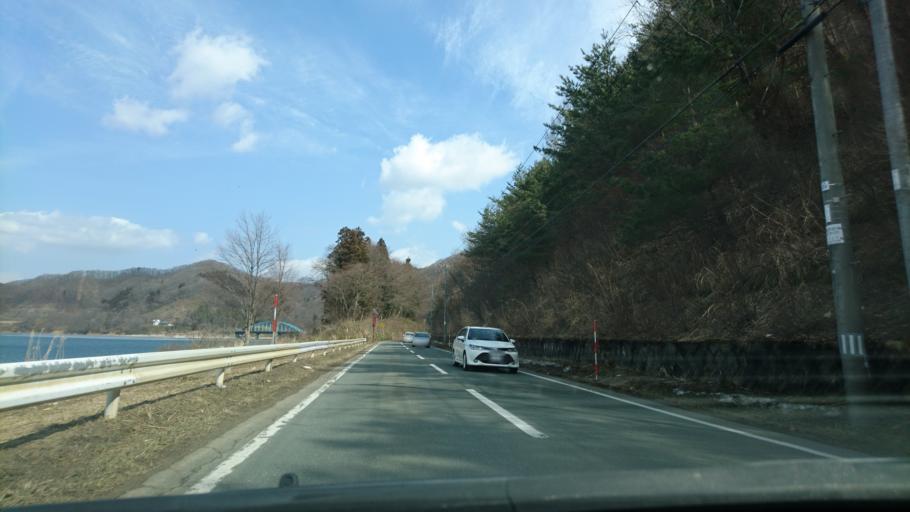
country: JP
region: Iwate
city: Shizukuishi
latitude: 39.6824
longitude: 141.0273
